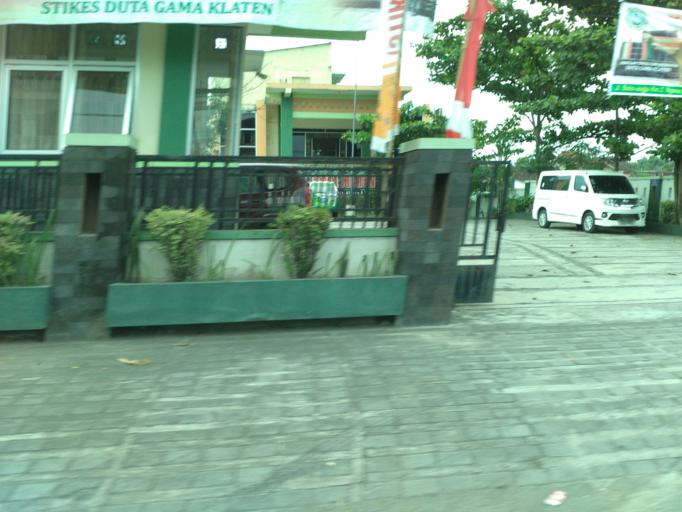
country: ID
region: Central Java
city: Klaten
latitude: -7.6863
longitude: 110.6385
